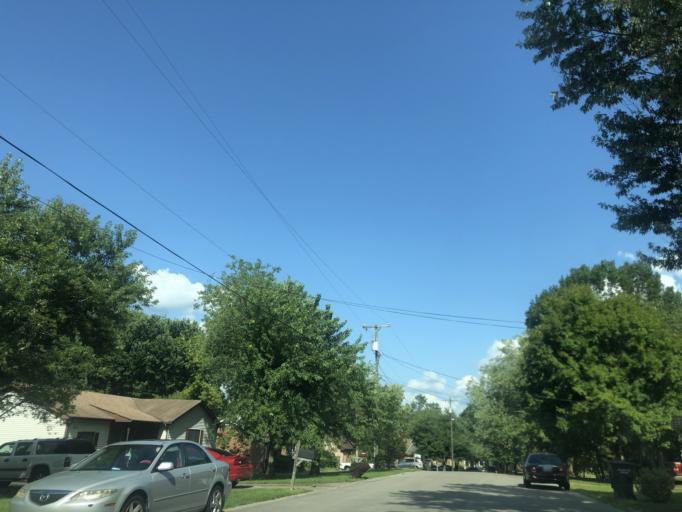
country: US
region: Tennessee
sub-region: Wilson County
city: Green Hill
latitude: 36.2054
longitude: -86.5981
